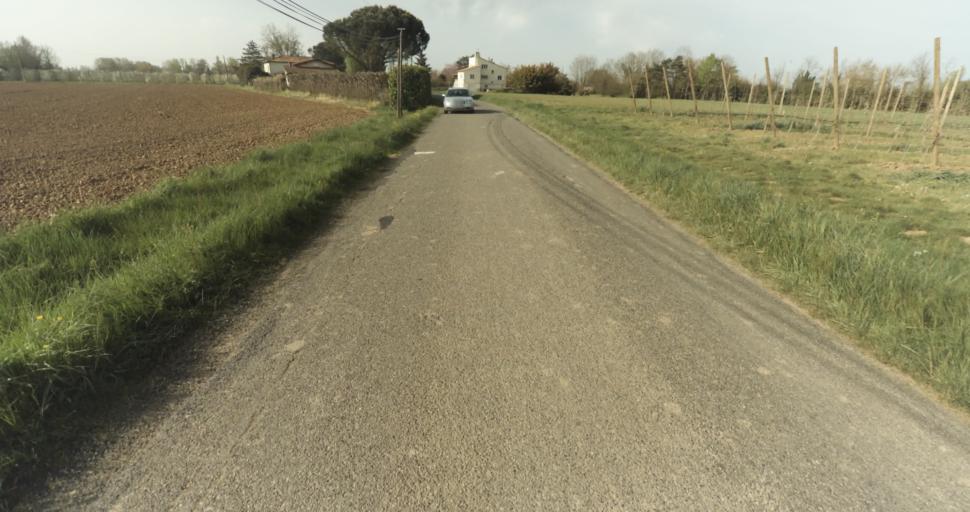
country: FR
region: Midi-Pyrenees
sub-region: Departement du Tarn-et-Garonne
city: Moissac
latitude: 44.1053
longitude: 1.1280
